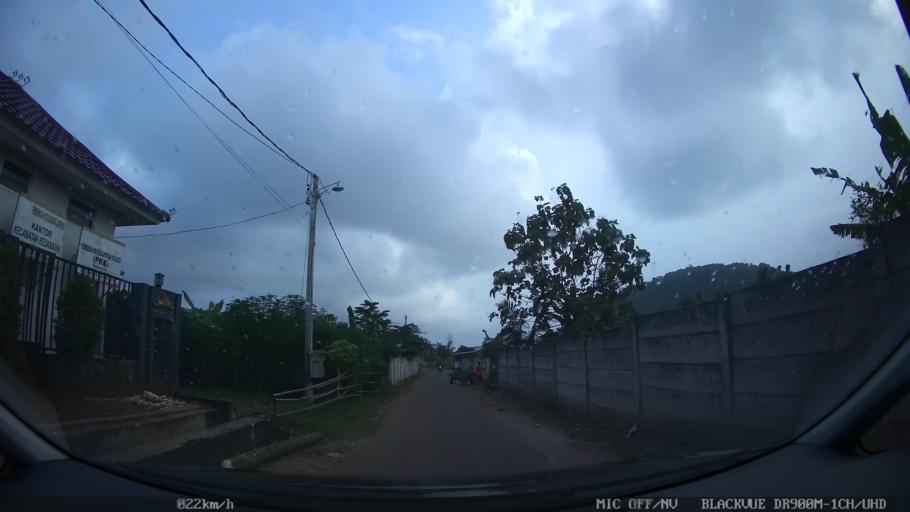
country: ID
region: Lampung
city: Bandarlampung
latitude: -5.4185
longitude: 105.2897
